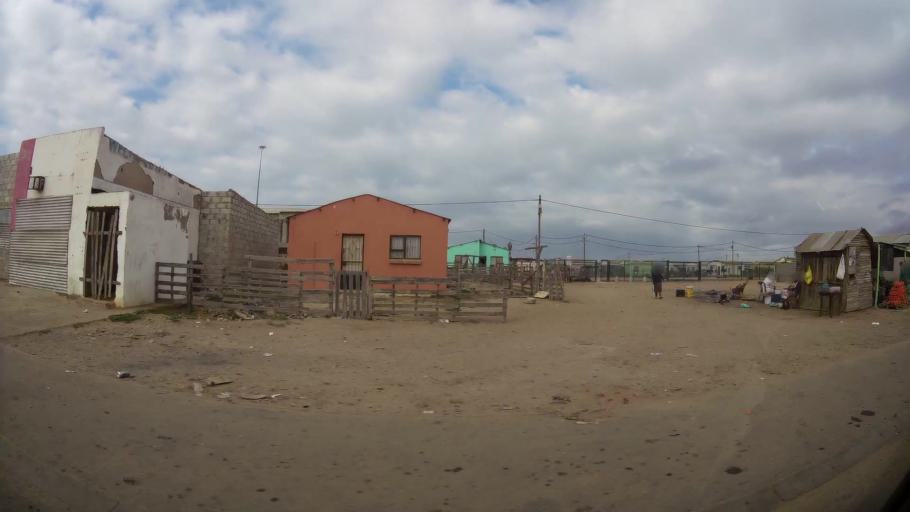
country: ZA
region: Eastern Cape
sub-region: Nelson Mandela Bay Metropolitan Municipality
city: Port Elizabeth
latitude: -33.8256
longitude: 25.6339
